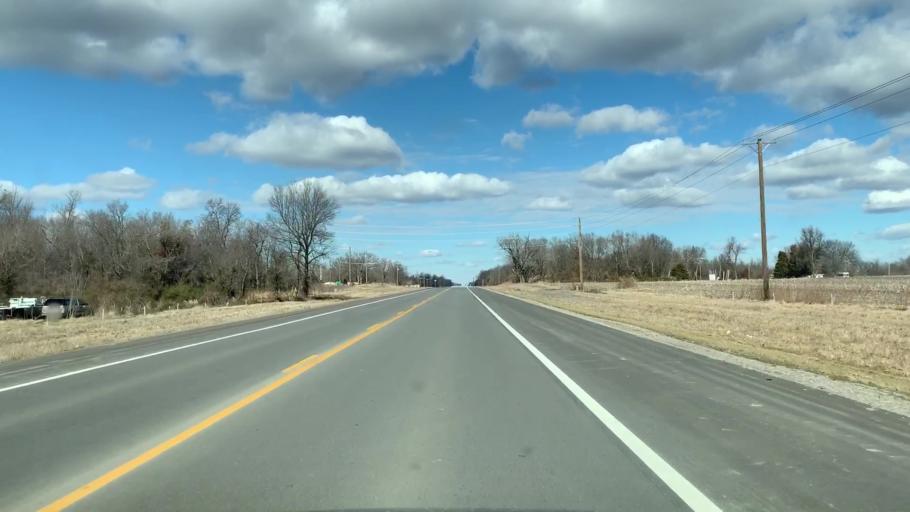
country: US
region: Kansas
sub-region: Cherokee County
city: Columbus
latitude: 37.2197
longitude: -94.8318
